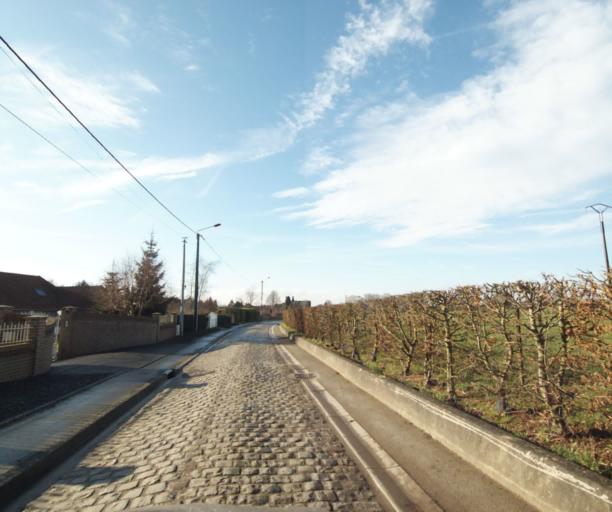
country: FR
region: Nord-Pas-de-Calais
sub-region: Departement du Nord
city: Preseau
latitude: 50.3124
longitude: 3.5823
